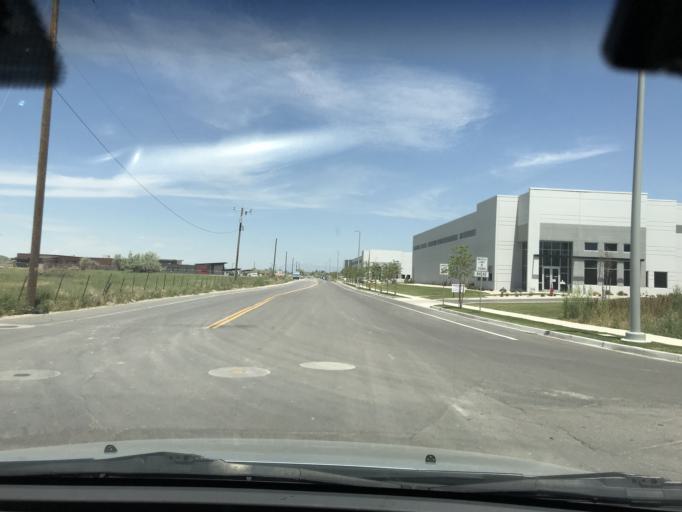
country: US
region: Utah
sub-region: Davis County
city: North Salt Lake
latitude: 40.8131
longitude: -111.9535
